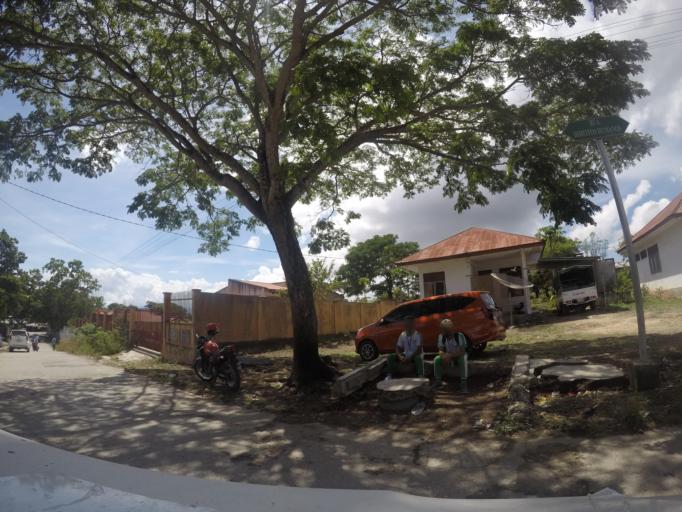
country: TL
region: Baucau
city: Baucau
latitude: -8.4734
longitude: 126.4570
